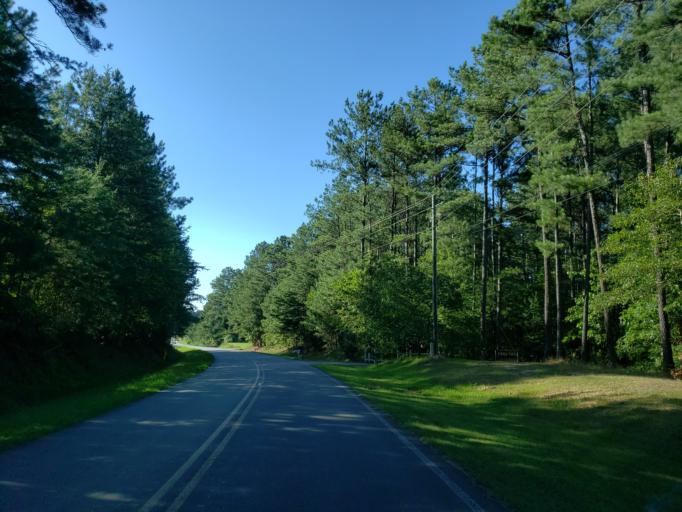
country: US
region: Georgia
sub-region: Bartow County
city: Euharlee
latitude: 34.1177
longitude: -85.0111
